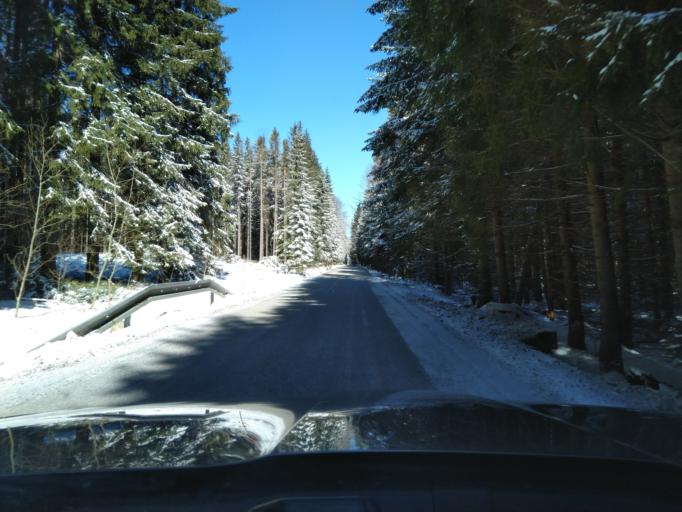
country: CZ
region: Jihocesky
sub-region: Okres Prachatice
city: Zdikov
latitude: 49.0514
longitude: 13.6611
